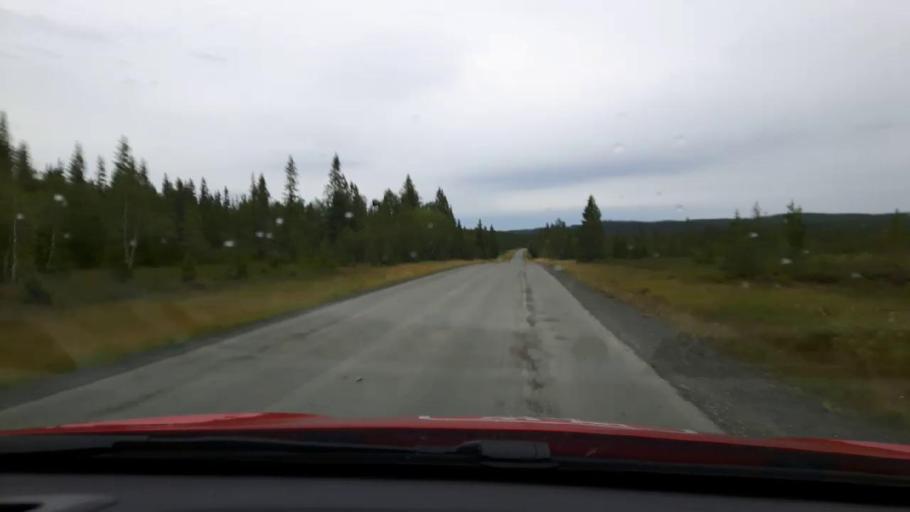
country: SE
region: Jaemtland
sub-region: Are Kommun
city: Are
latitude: 63.4419
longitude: 13.2464
